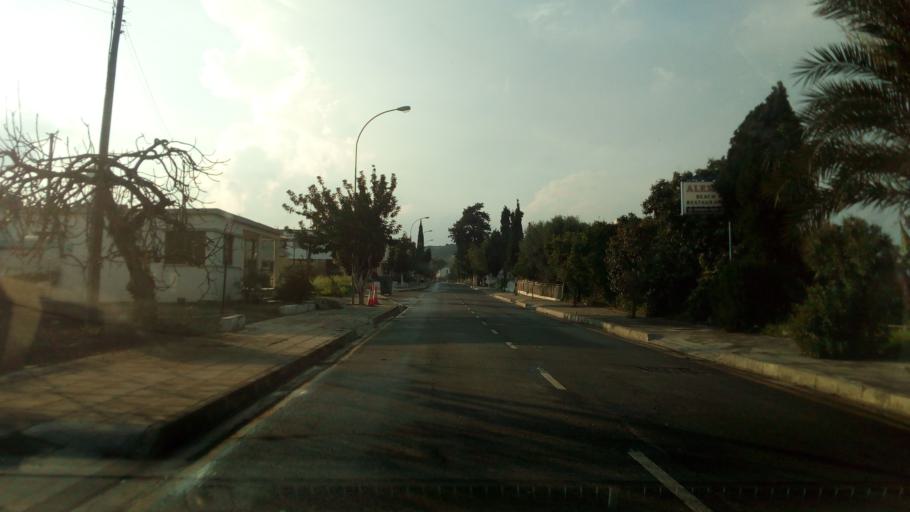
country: CY
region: Lefkosia
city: Kato Pyrgos
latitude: 35.1861
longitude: 32.6781
